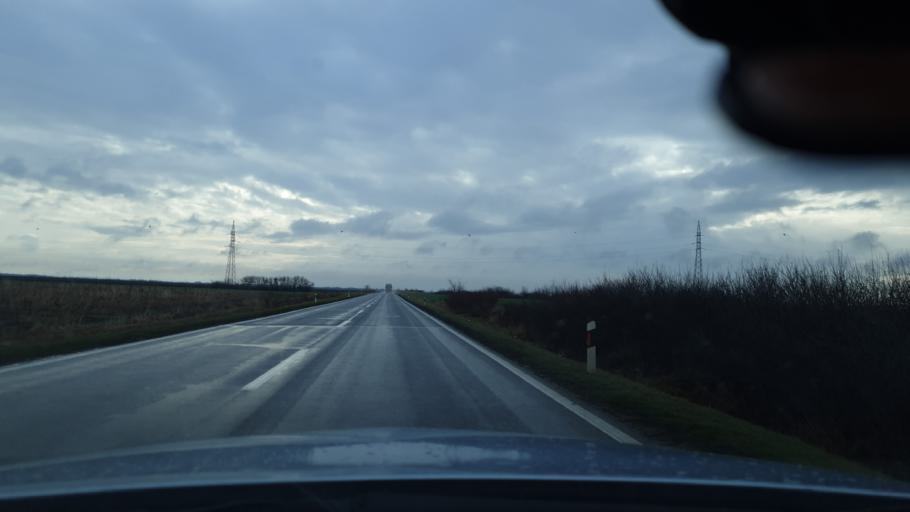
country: RS
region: Autonomna Pokrajina Vojvodina
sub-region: Juznobanatski Okrug
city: Kovin
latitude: 44.7976
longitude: 20.9071
